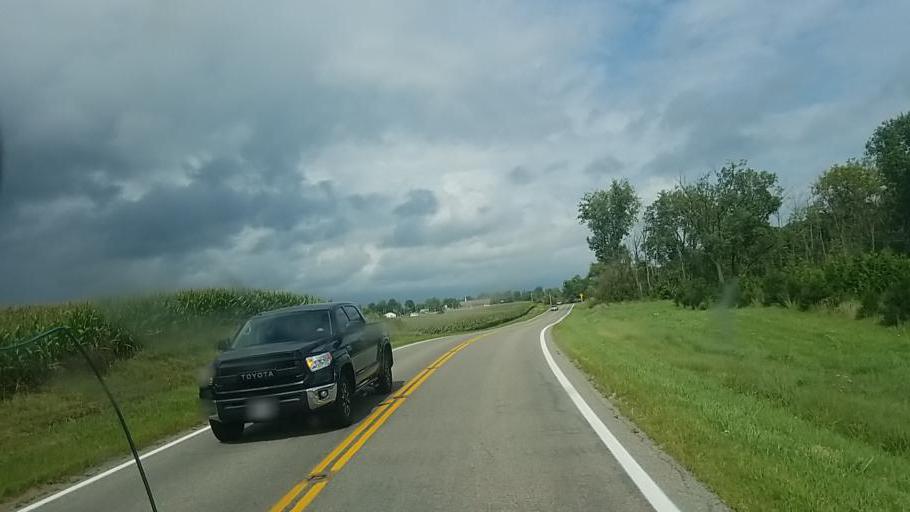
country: US
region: Ohio
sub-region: Champaign County
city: North Lewisburg
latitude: 40.2855
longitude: -83.5894
